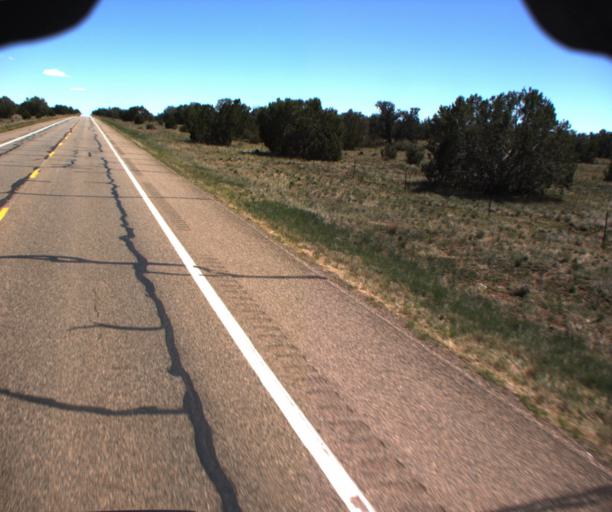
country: US
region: Arizona
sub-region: Coconino County
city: Williams
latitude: 35.1848
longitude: -112.4672
